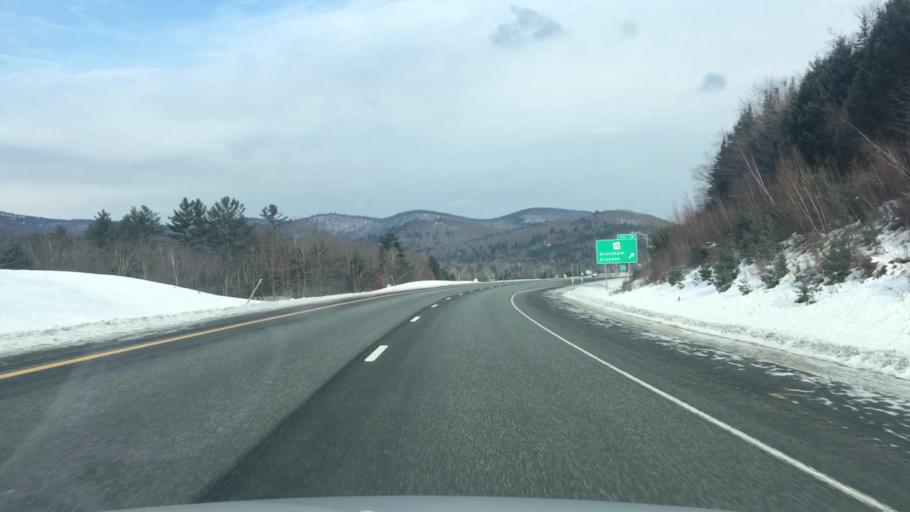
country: US
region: New Hampshire
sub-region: Sullivan County
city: Grantham
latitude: 43.4935
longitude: -72.1305
